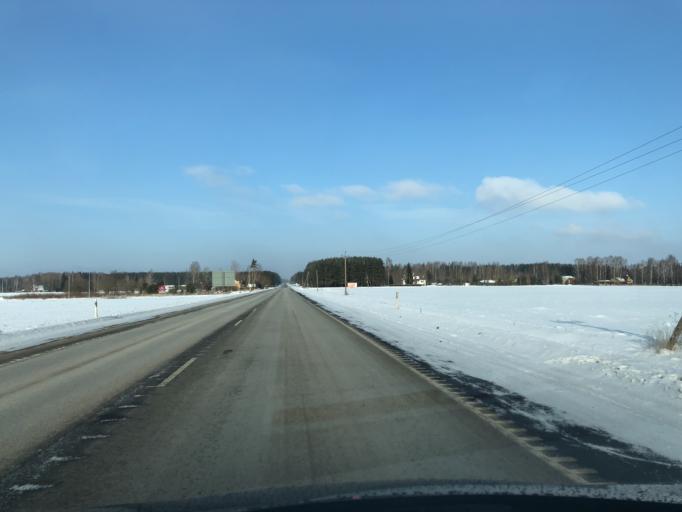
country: EE
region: Tartu
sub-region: Tartu linn
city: Tartu
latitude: 58.3812
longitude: 26.6742
